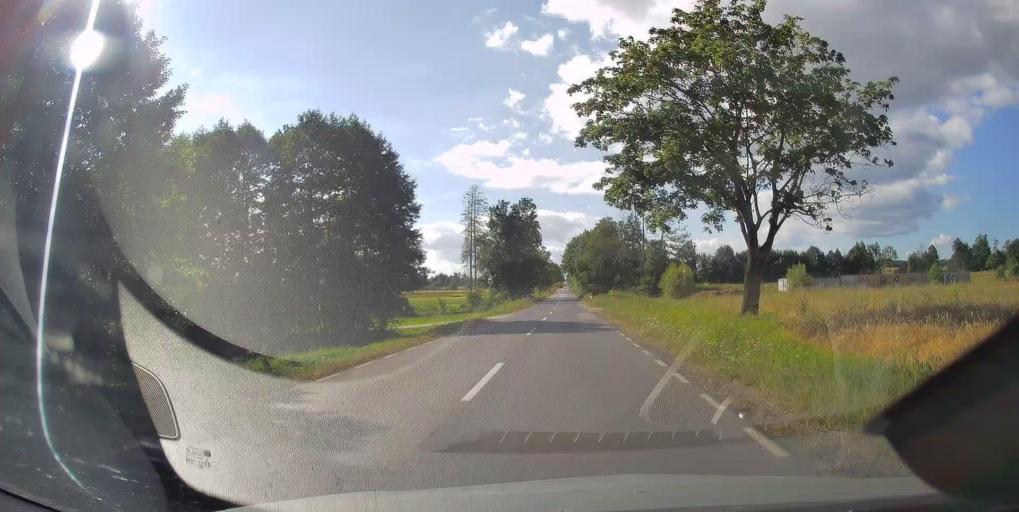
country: PL
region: Swietokrzyskie
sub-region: Powiat kielecki
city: Bodzentyn
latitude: 50.9603
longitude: 20.9053
